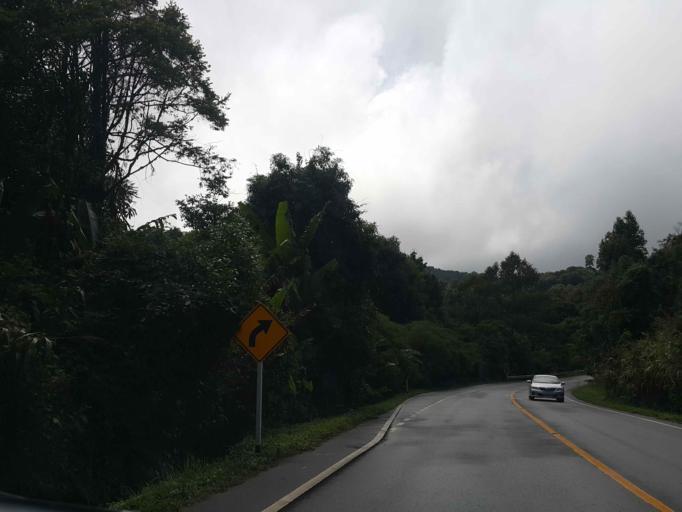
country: TH
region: Chiang Mai
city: Mae Chaem
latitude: 18.5129
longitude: 98.5056
